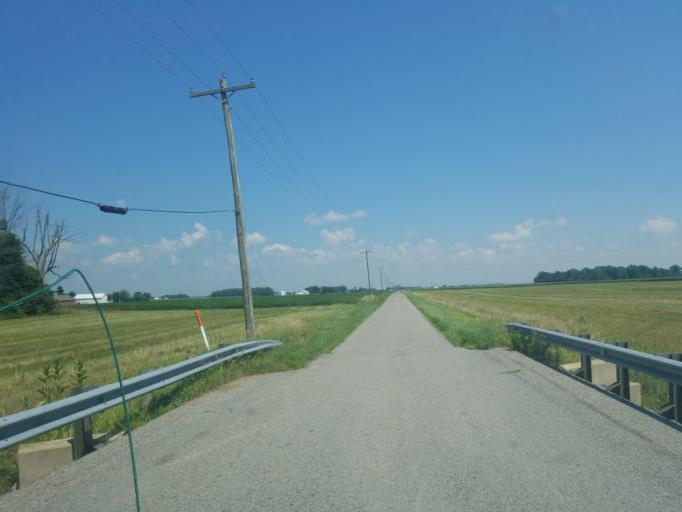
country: US
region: Ohio
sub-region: Shelby County
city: Jackson Center
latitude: 40.4106
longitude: -84.0653
